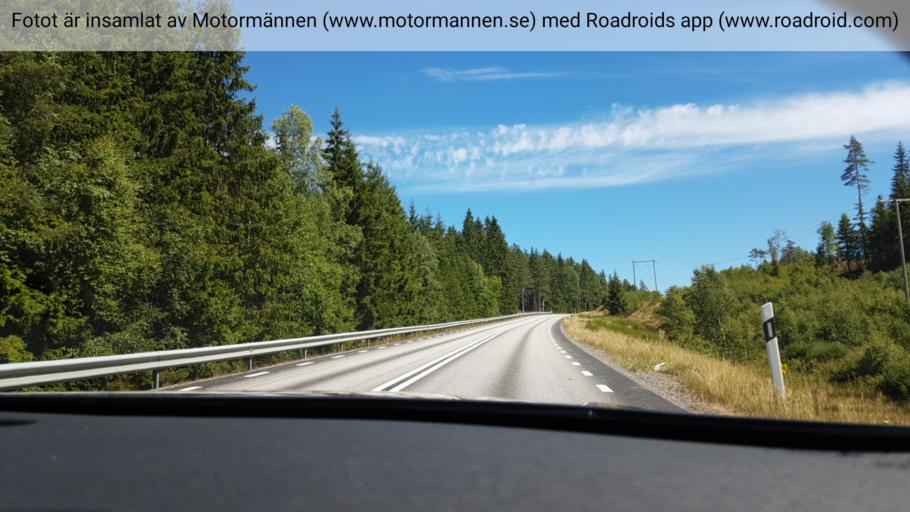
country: SE
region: Joenkoeping
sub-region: Gnosjo Kommun
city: Gnosjoe
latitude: 57.3397
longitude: 13.7801
